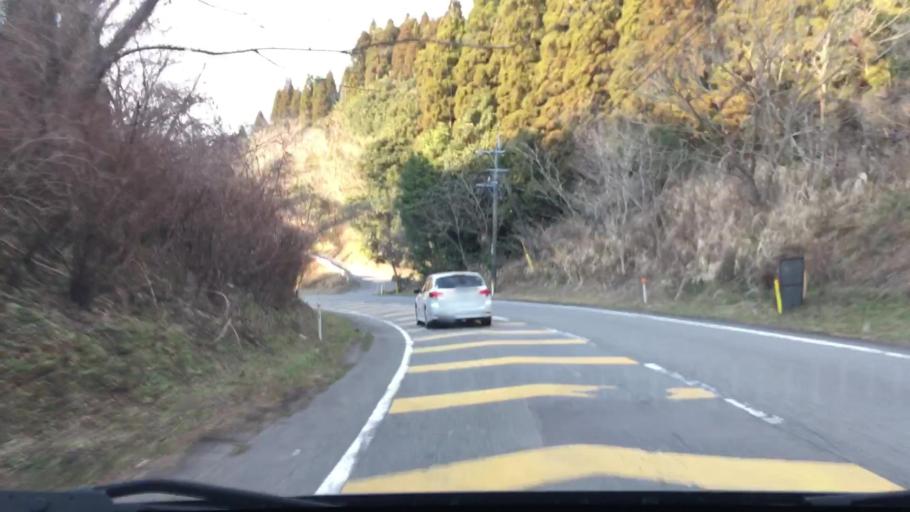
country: JP
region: Miyazaki
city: Miyazaki-shi
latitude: 31.7895
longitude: 131.3201
